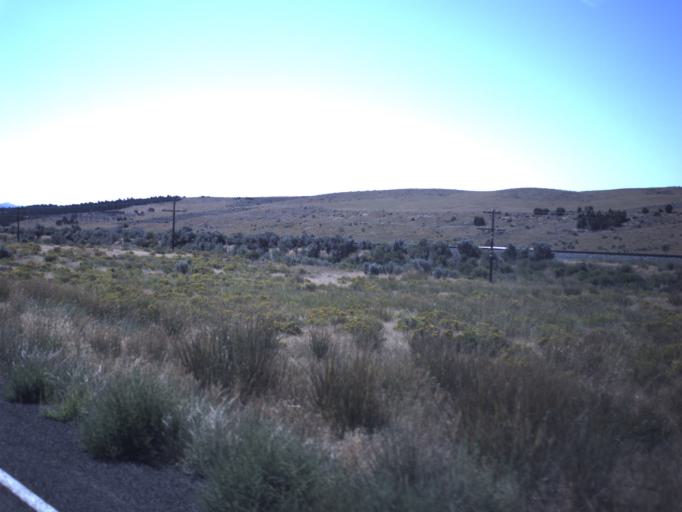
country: US
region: Utah
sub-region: Utah County
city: Genola
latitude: 39.9510
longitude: -112.2368
